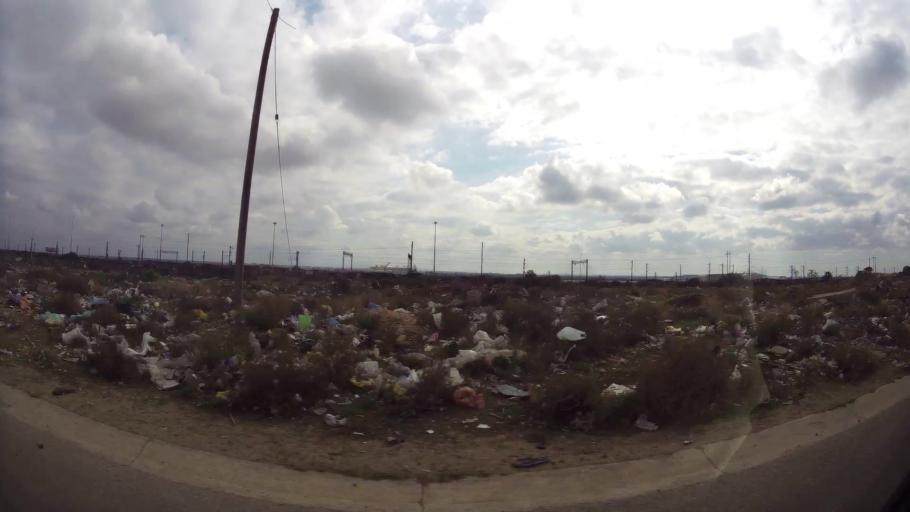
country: ZA
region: Eastern Cape
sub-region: Nelson Mandela Bay Metropolitan Municipality
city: Port Elizabeth
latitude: -33.8217
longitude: 25.6269
